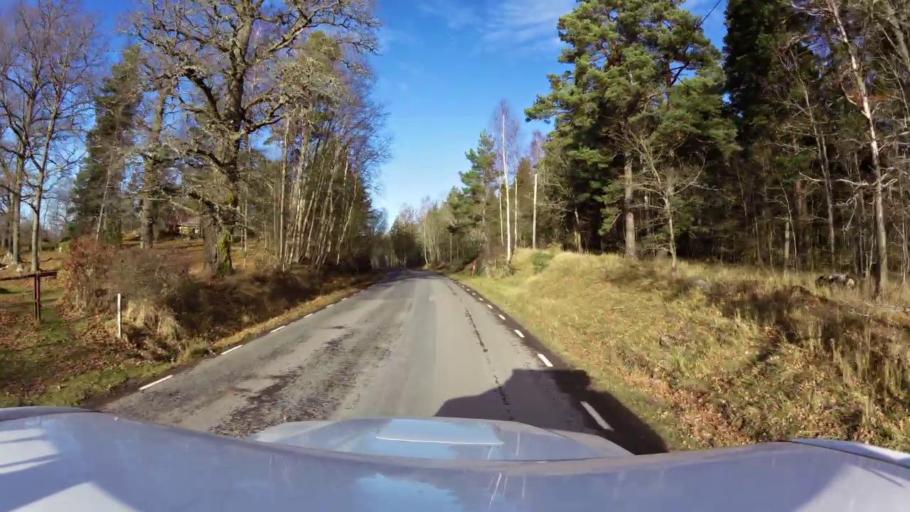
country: SE
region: OEstergoetland
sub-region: Linkopings Kommun
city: Linkoping
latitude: 58.3724
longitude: 15.6267
